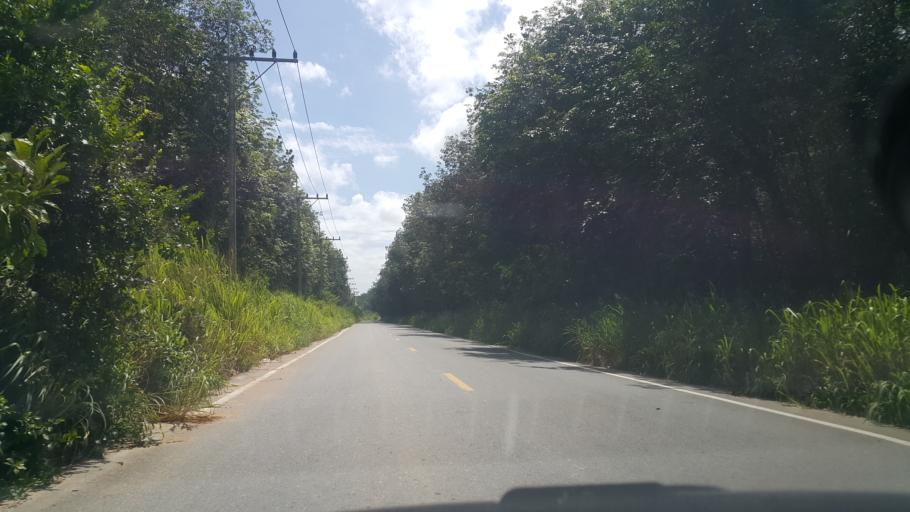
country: TH
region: Rayong
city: Ban Chang
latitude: 12.8092
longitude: 100.9995
